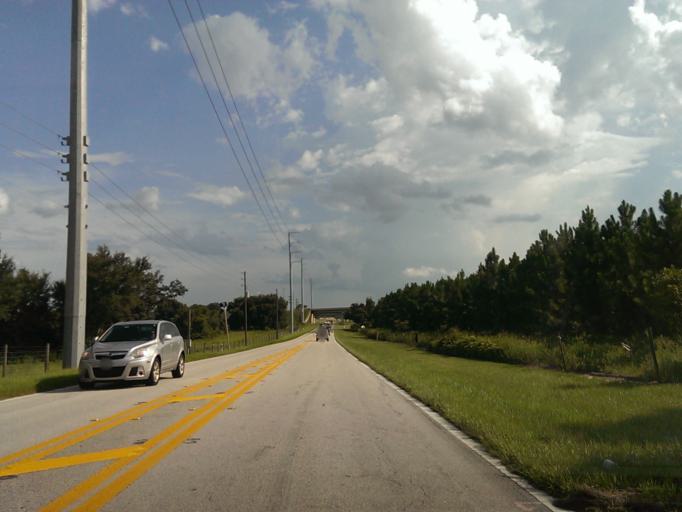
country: US
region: Florida
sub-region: Polk County
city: Citrus Ridge
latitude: 28.4402
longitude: -81.6366
